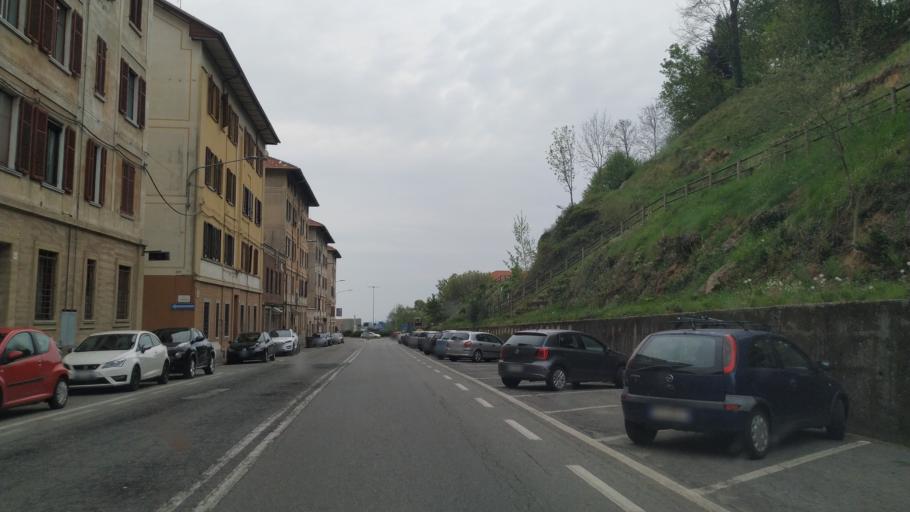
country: IT
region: Piedmont
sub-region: Provincia di Biella
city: Occhieppo Inferiore
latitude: 45.5574
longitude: 8.0275
